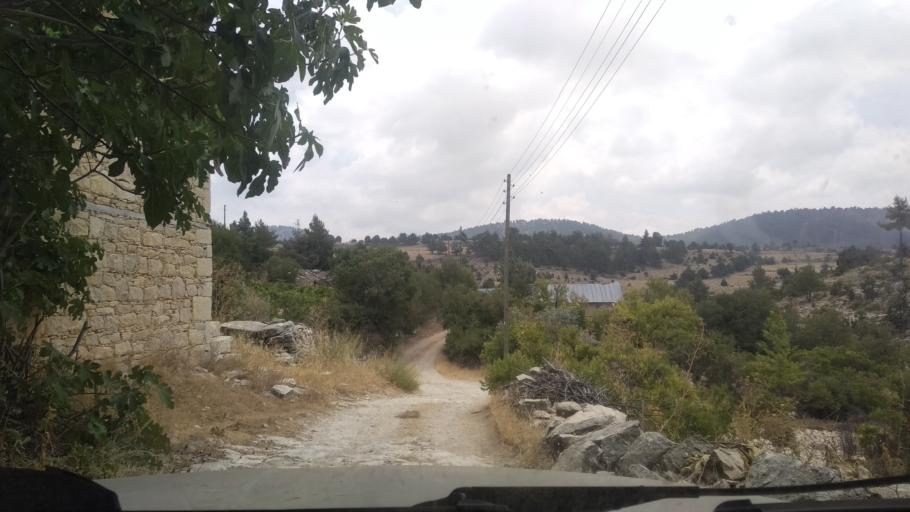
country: TR
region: Mersin
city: Sarikavak
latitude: 36.6000
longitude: 33.7265
